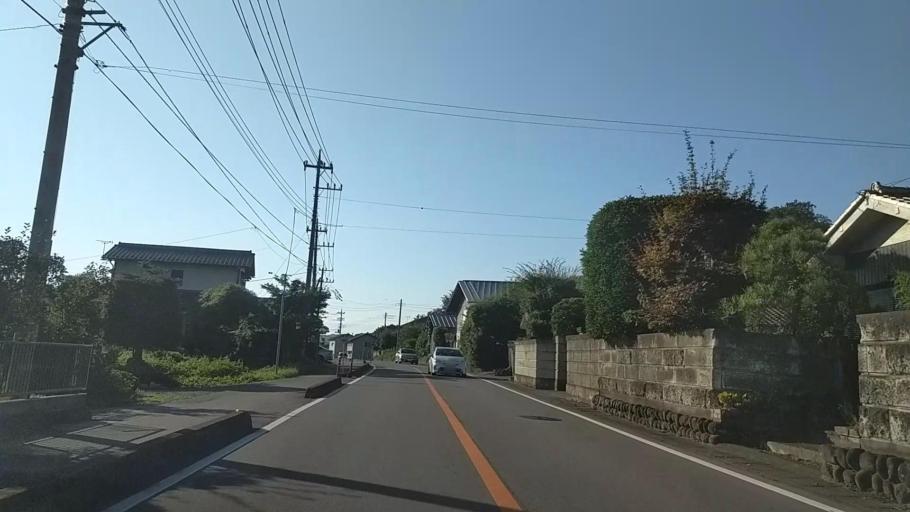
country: JP
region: Gunma
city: Annaka
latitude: 36.3442
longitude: 138.8827
